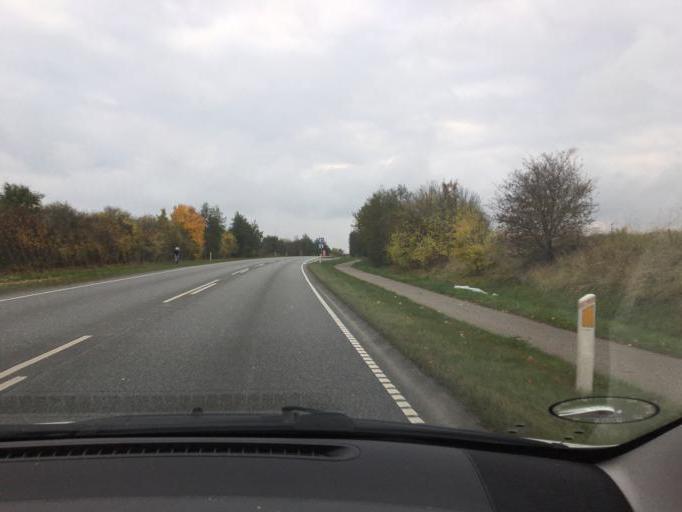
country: DK
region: South Denmark
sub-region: Fredericia Kommune
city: Fredericia
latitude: 55.6056
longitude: 9.7577
